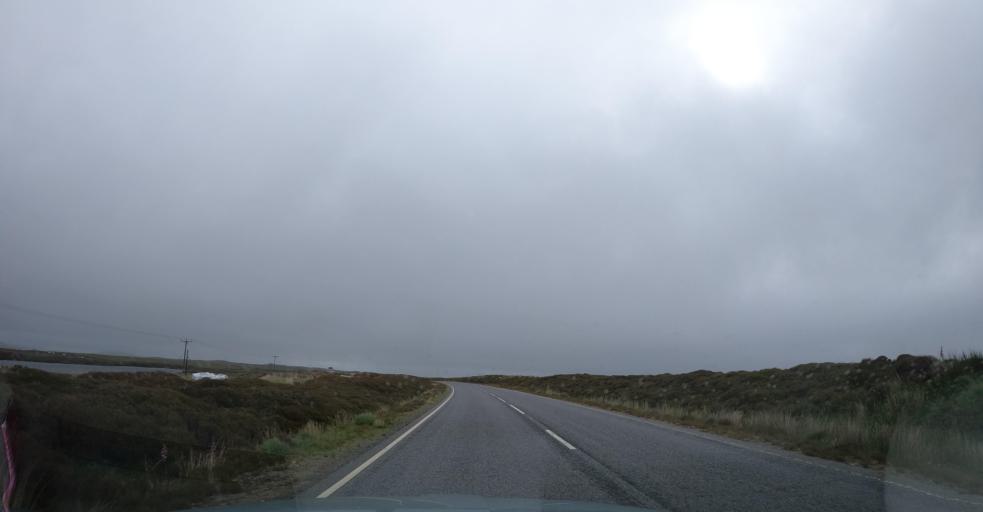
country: GB
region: Scotland
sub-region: Eilean Siar
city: Isle of North Uist
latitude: 57.5729
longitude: -7.2738
